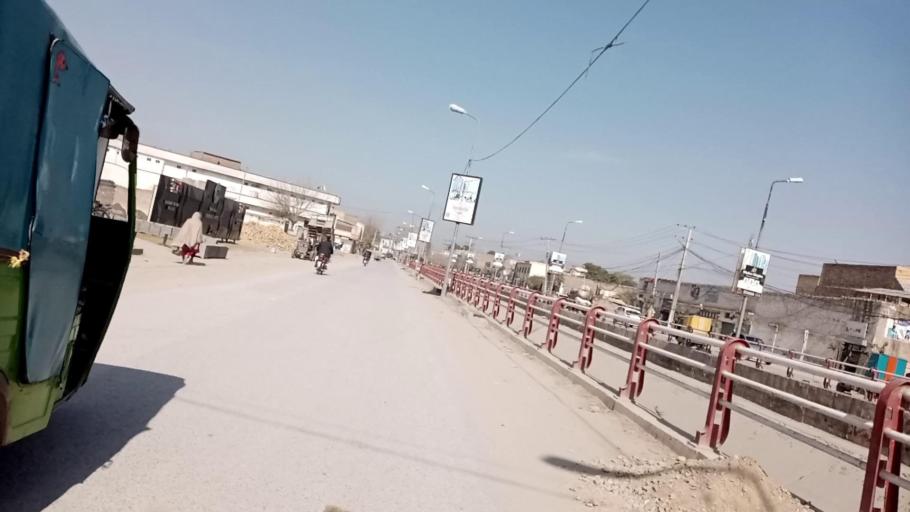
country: PK
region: Khyber Pakhtunkhwa
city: Peshawar
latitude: 33.9854
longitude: 71.4984
